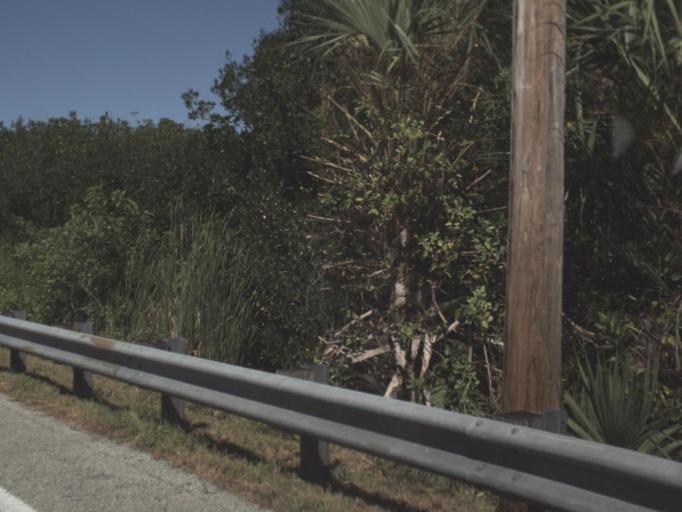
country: US
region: Florida
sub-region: Collier County
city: Marco
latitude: 25.9366
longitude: -81.4571
